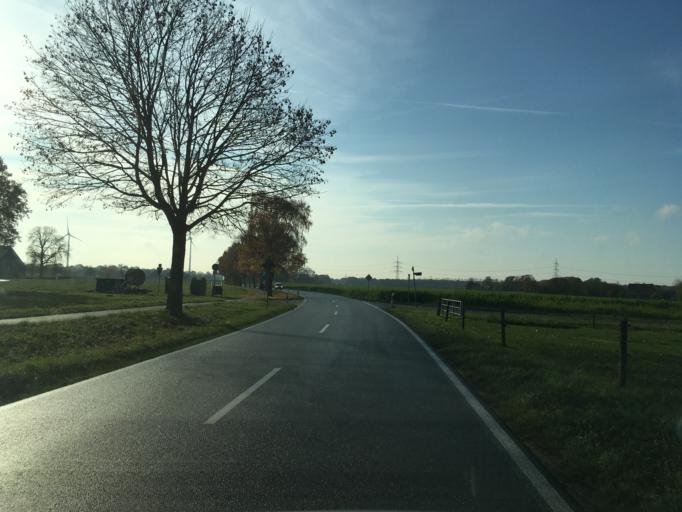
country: DE
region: North Rhine-Westphalia
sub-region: Regierungsbezirk Munster
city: Ahaus
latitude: 52.0453
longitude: 6.9725
